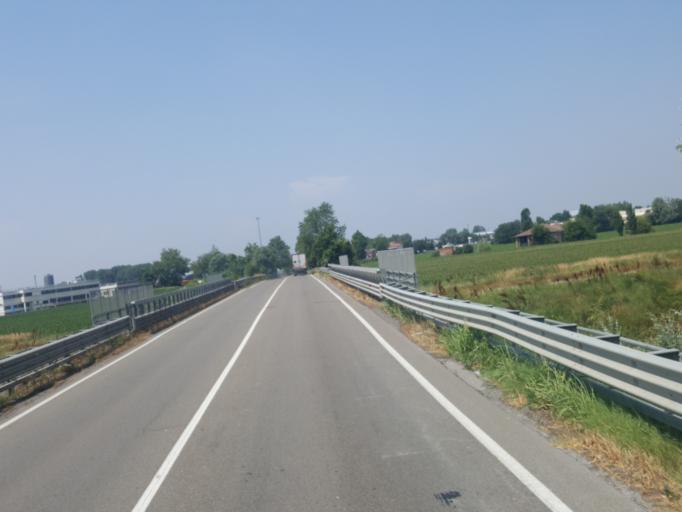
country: IT
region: Emilia-Romagna
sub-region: Provincia di Bologna
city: Anzola dell'Emilia
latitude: 44.5525
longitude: 11.1825
